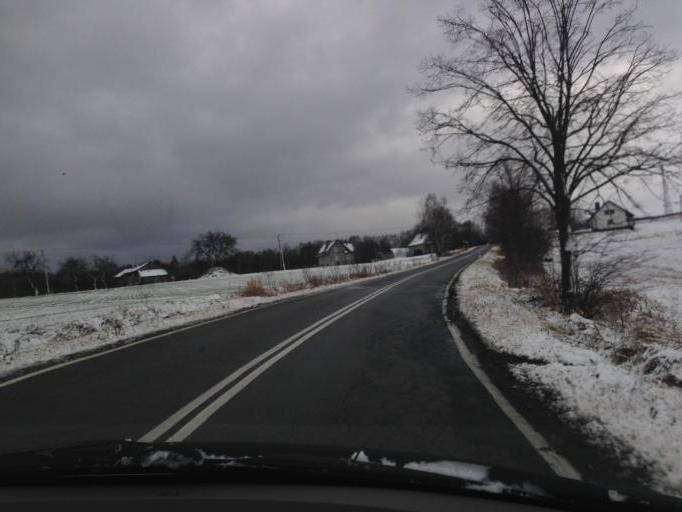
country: PL
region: Lesser Poland Voivodeship
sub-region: Powiat brzeski
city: Iwkowa
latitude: 49.8579
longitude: 20.5710
